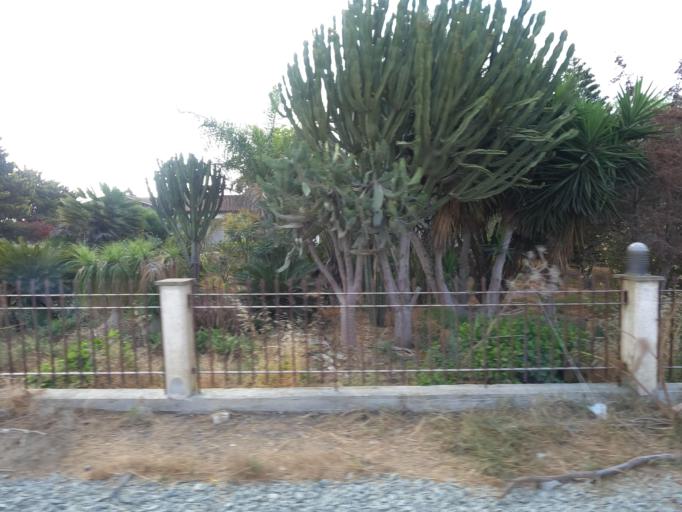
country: CY
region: Larnaka
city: Tersefanou
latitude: 34.8291
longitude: 33.5544
